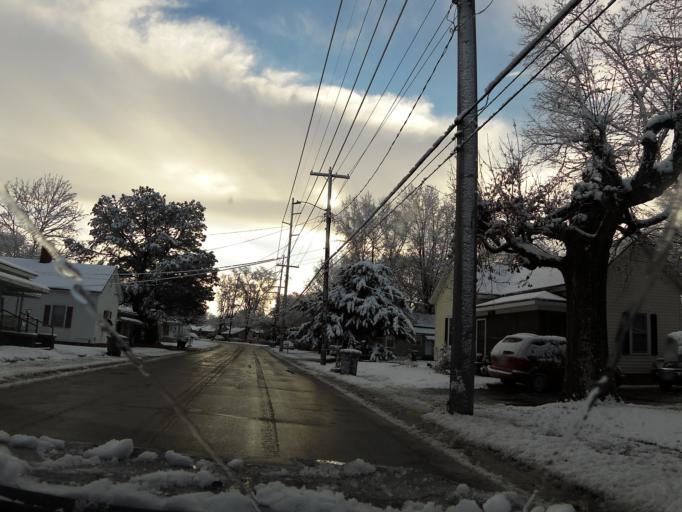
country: US
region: North Carolina
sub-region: Nash County
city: Rocky Mount
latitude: 35.9275
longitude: -77.8129
